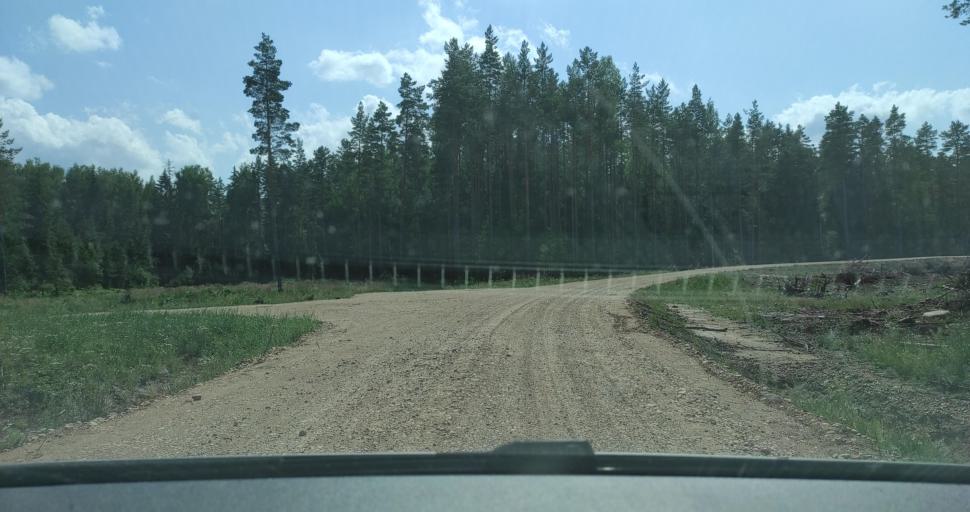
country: LV
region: Kuldigas Rajons
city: Kuldiga
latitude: 57.0623
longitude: 22.1942
